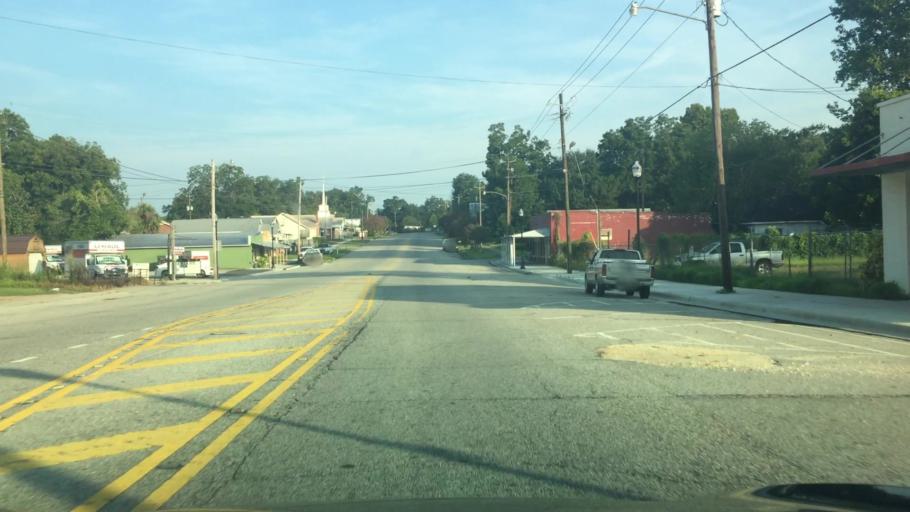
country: US
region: Alabama
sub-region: Covington County
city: Florala
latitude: 31.0069
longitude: -86.3303
